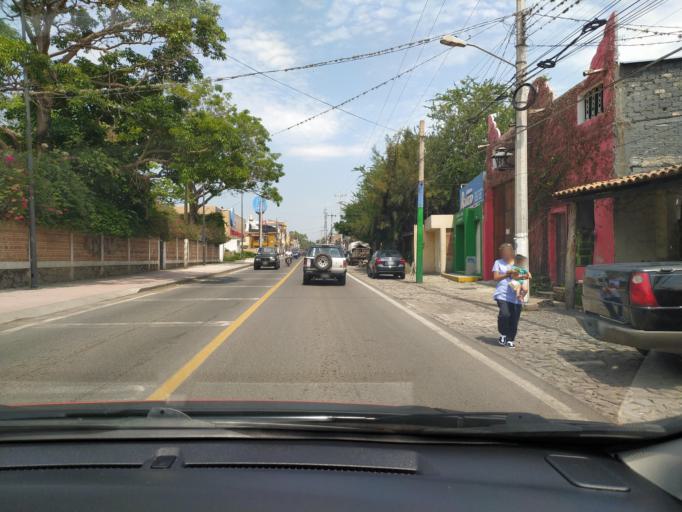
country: MX
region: Jalisco
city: San Juan Cosala
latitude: 20.2887
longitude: -103.3446
